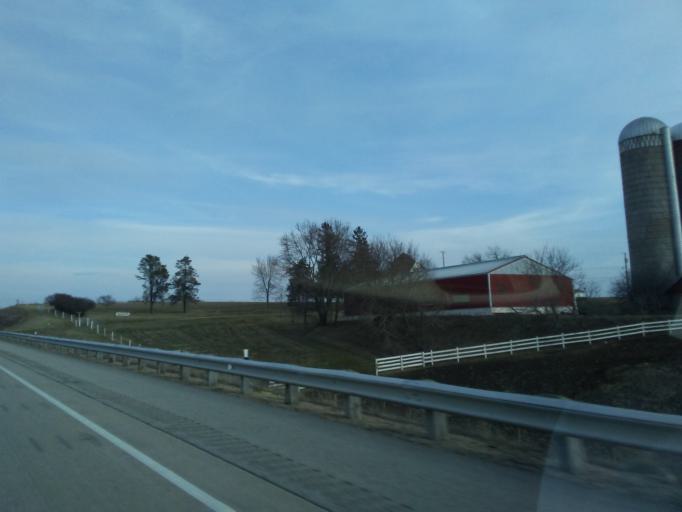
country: US
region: Wisconsin
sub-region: Iowa County
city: Barneveld
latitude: 43.0094
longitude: -89.8667
